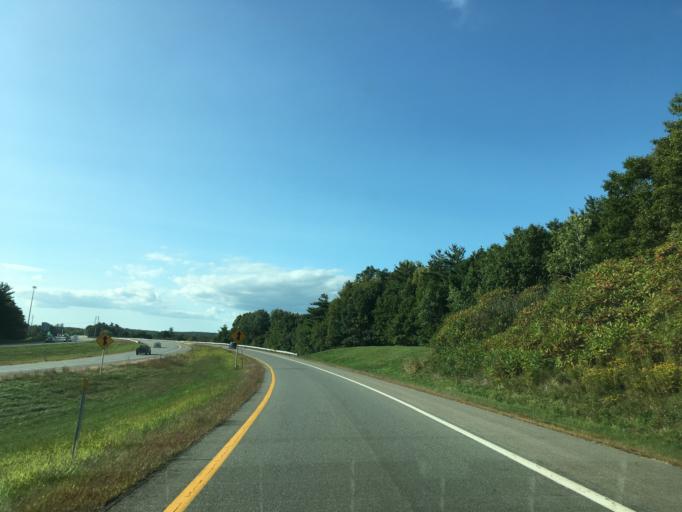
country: US
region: New Hampshire
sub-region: Rockingham County
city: Hampton
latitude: 42.9573
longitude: -70.8529
